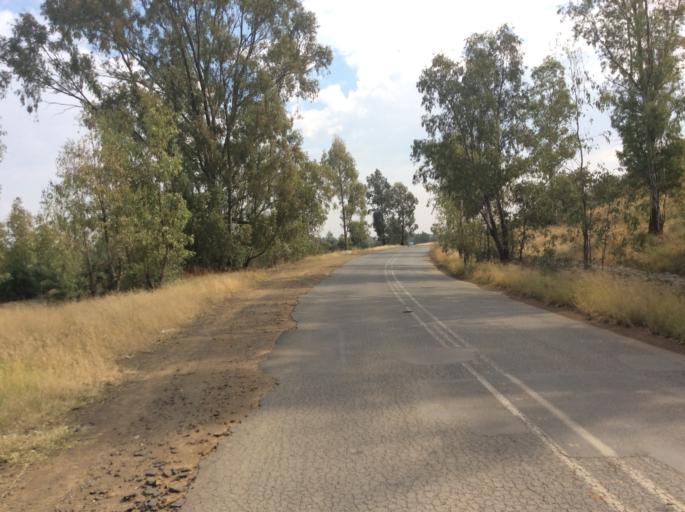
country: LS
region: Mafeteng
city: Mafeteng
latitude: -29.7348
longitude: 27.0467
